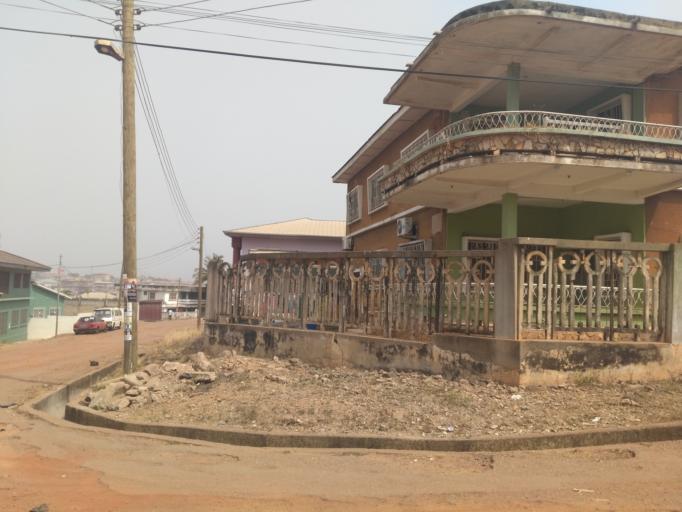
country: GH
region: Ashanti
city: Kumasi
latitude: 6.6837
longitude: -1.5994
